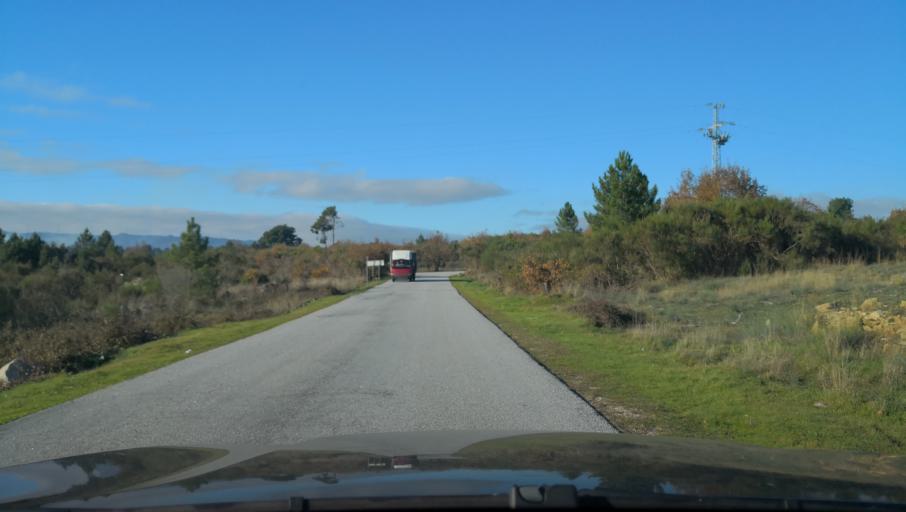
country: PT
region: Vila Real
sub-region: Vila Real
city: Vila Real
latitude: 41.3440
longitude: -7.6633
